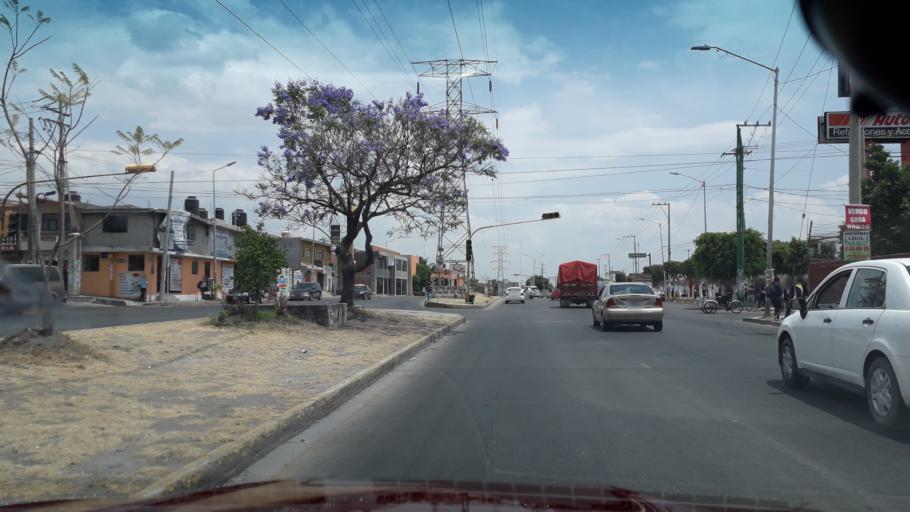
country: MX
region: Puebla
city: Puebla
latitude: 19.0019
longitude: -98.2309
